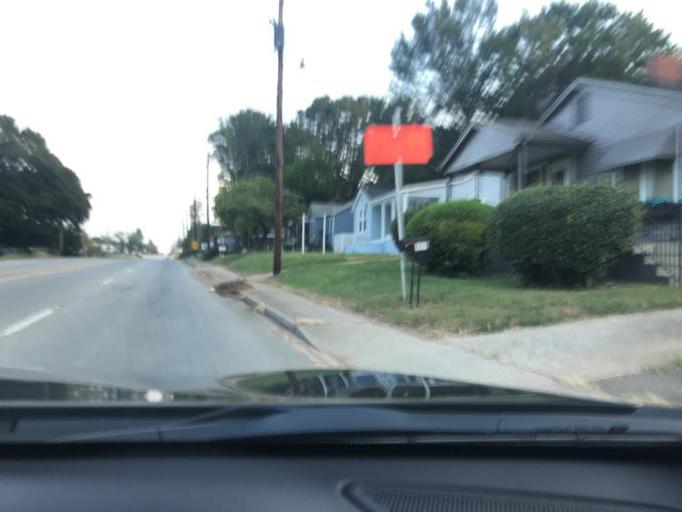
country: US
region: South Carolina
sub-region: Greenville County
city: Welcome
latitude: 34.8305
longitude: -82.4385
